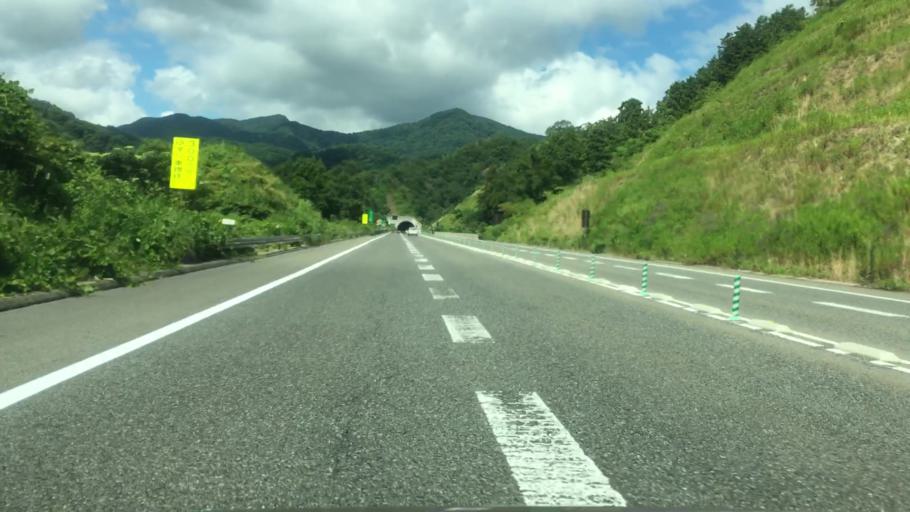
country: JP
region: Hyogo
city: Toyooka
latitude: 35.6292
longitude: 134.6177
